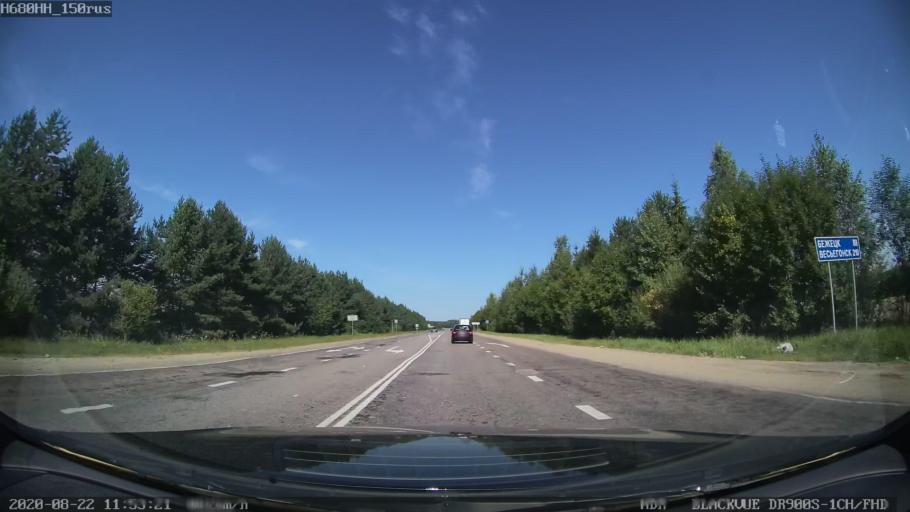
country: RU
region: Tverskaya
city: Vasil'yevskiy Mokh
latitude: 57.1259
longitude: 36.1117
